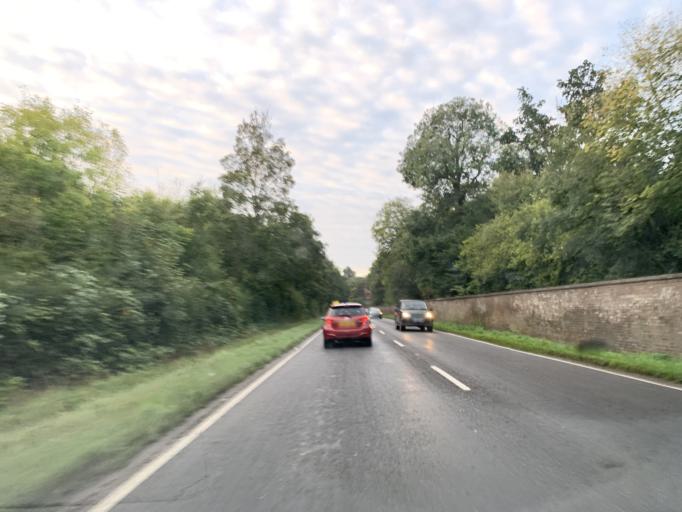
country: GB
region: England
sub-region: Hampshire
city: Romsey
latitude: 50.9797
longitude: -1.4859
